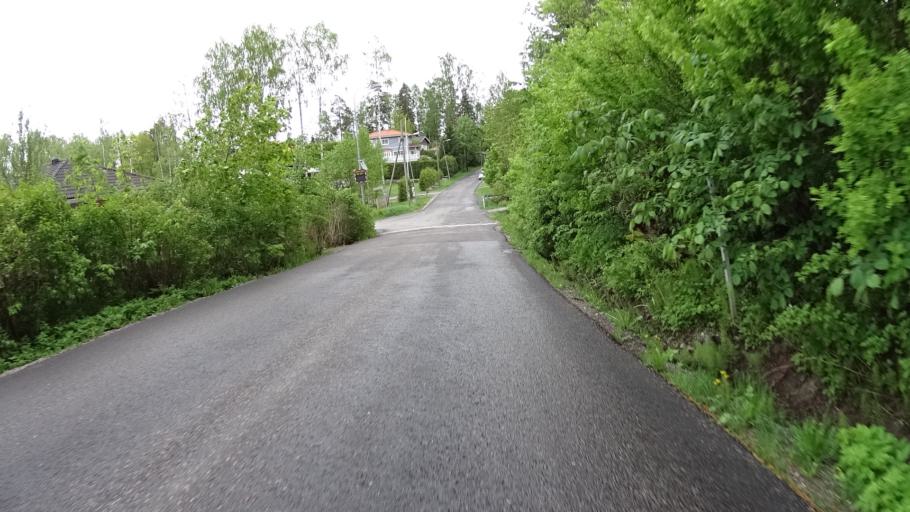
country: FI
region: Uusimaa
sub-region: Helsinki
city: Kauniainen
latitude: 60.2219
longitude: 24.7226
